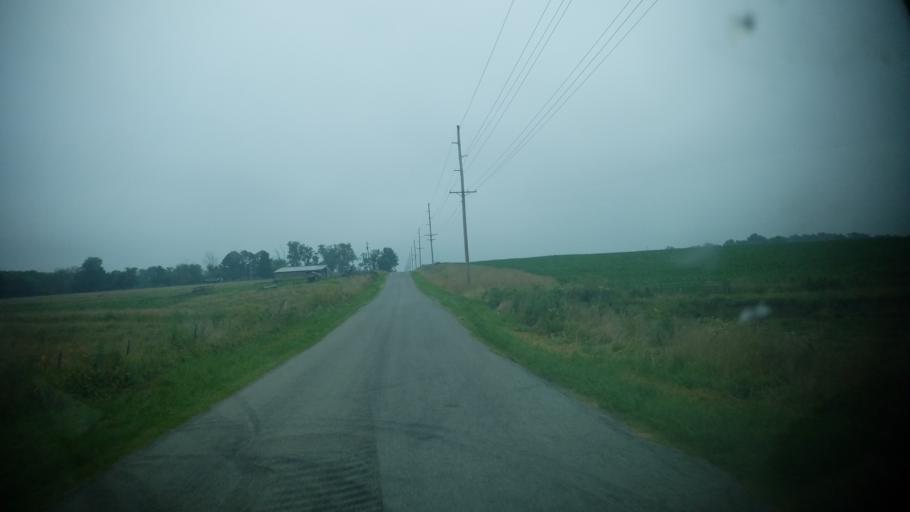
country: US
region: Illinois
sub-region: Clay County
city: Flora
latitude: 38.5340
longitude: -88.4022
